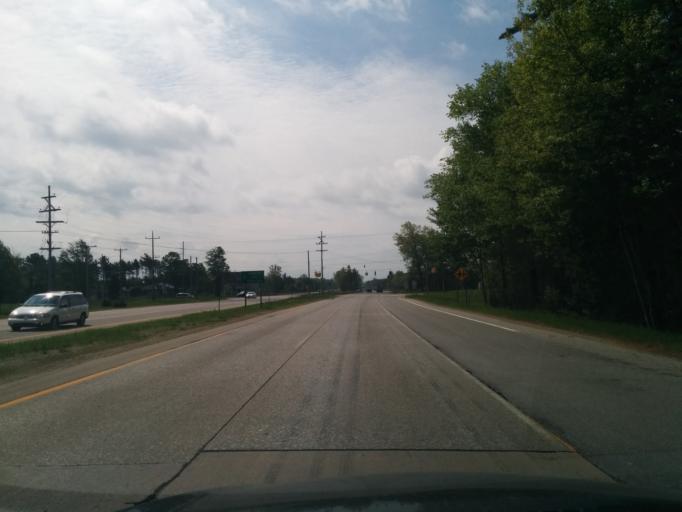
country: US
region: Michigan
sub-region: Ottawa County
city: Grand Haven
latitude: 43.0098
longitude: -86.2063
